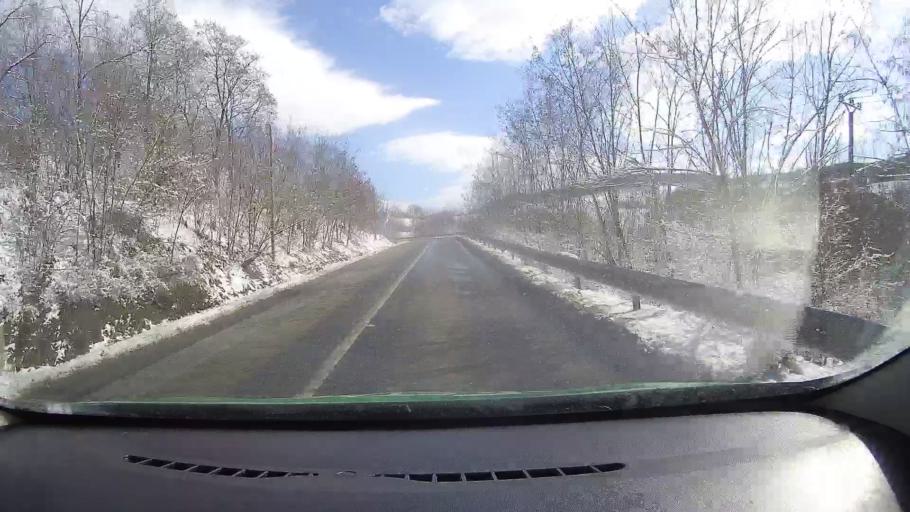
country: RO
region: Sibiu
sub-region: Comuna Barghis
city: Barghis
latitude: 45.9839
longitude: 24.5067
